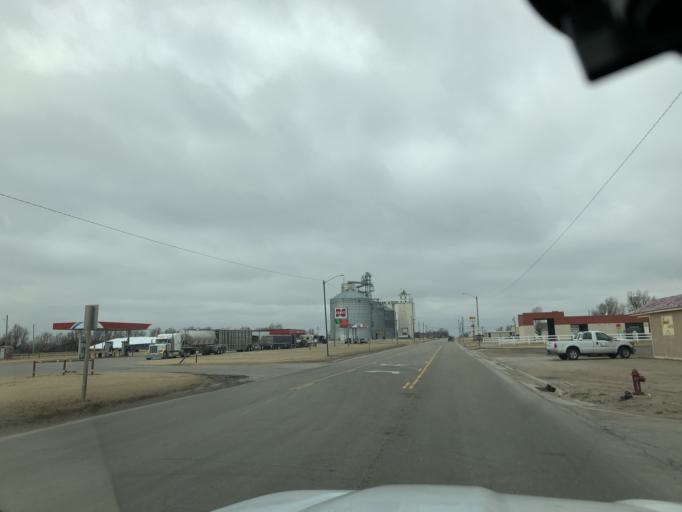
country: US
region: Kansas
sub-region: Stafford County
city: Stafford
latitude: 37.9548
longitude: -98.5932
